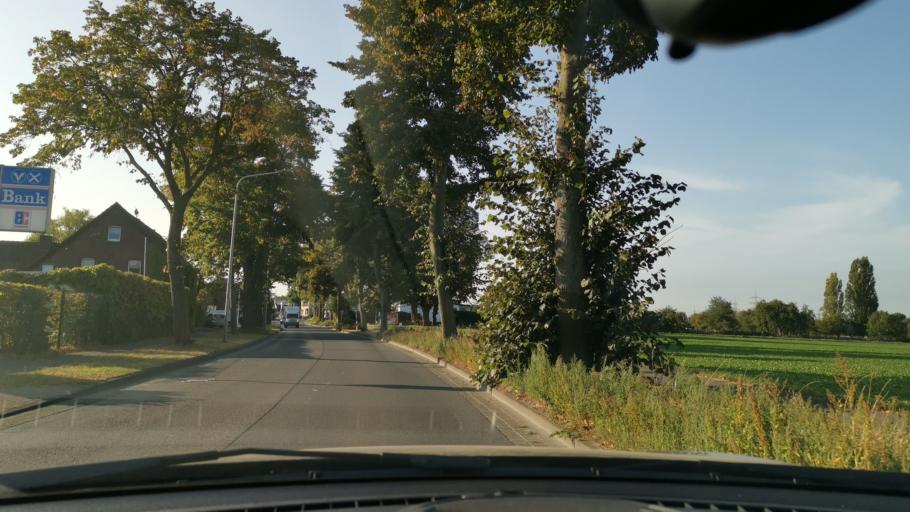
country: DE
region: North Rhine-Westphalia
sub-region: Regierungsbezirk Dusseldorf
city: Rommerskirchen
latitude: 51.1049
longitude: 6.7170
